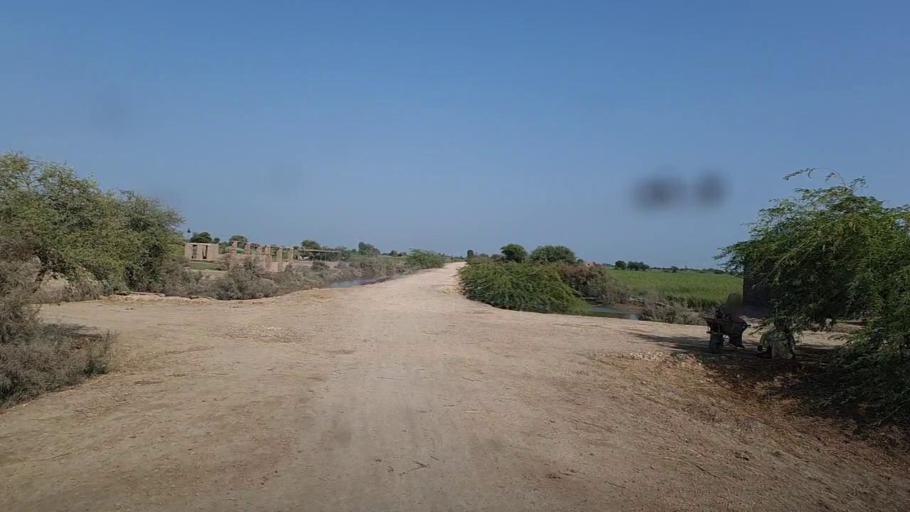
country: PK
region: Sindh
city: Kario
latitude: 24.7510
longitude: 68.4639
